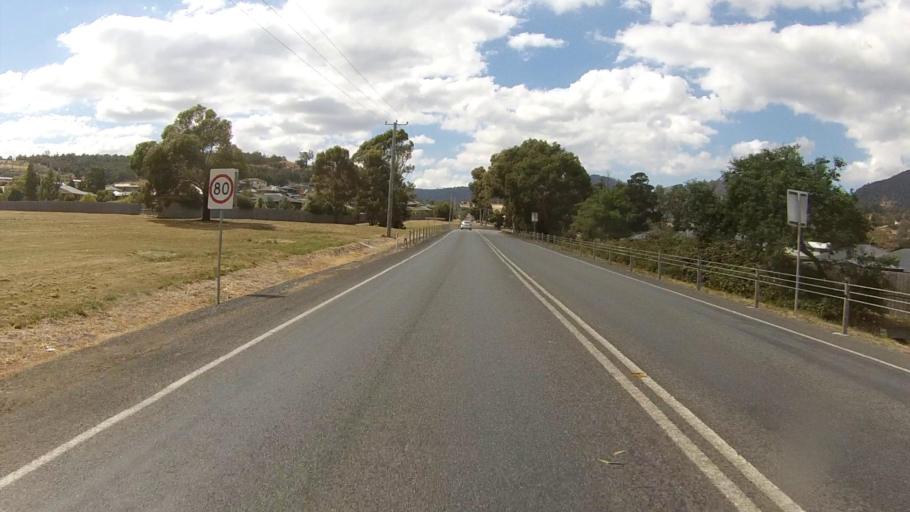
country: AU
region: Tasmania
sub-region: Brighton
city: Old Beach
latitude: -42.7778
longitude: 147.2791
